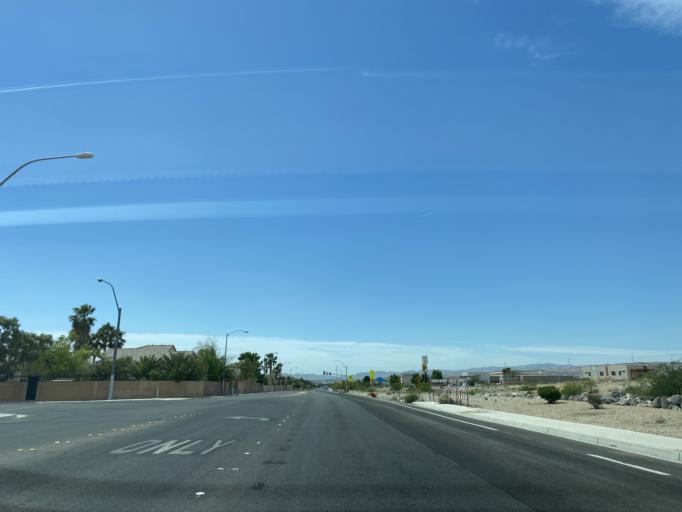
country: US
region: Nevada
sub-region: Clark County
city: Spring Valley
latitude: 36.1226
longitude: -115.2700
